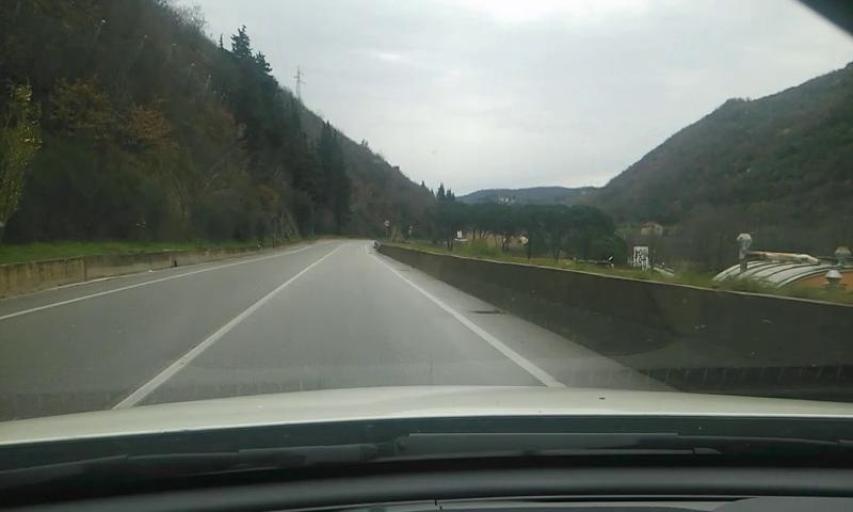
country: IT
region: Tuscany
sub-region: Provincia di Prato
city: Vaiano
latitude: 43.9156
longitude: 11.1252
